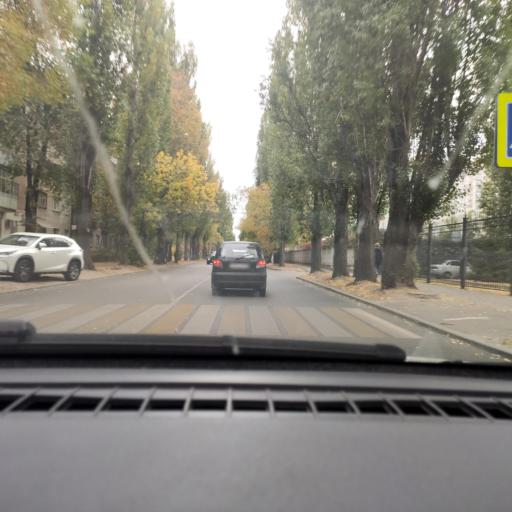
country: RU
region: Voronezj
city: Voronezh
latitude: 51.6850
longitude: 39.2572
